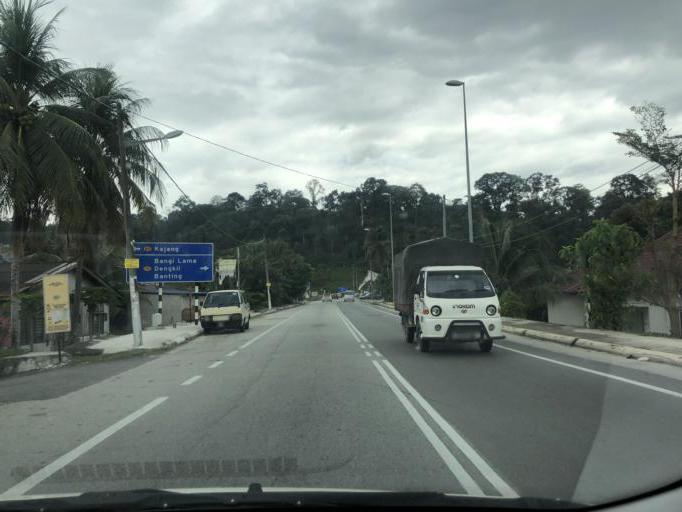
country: MY
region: Putrajaya
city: Putrajaya
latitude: 2.9191
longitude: 101.7581
